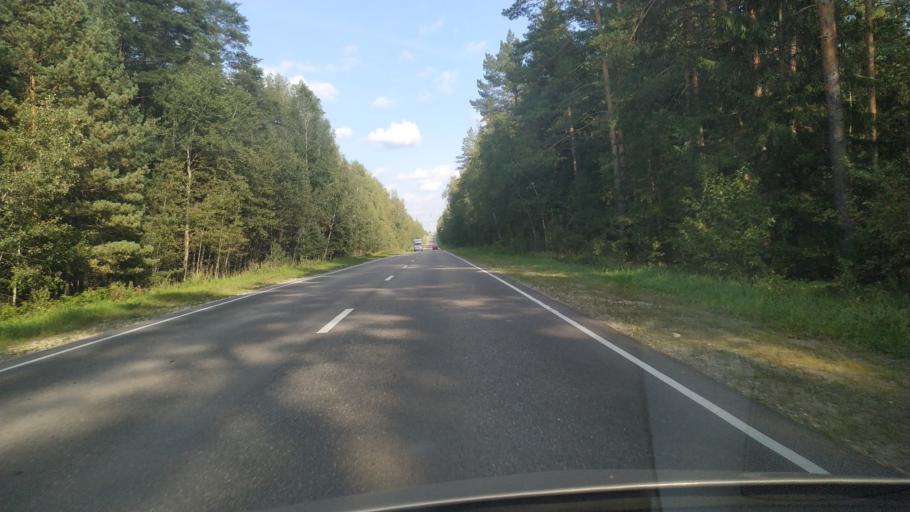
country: RU
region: Moskovskaya
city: Vereya
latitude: 55.7022
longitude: 39.2080
